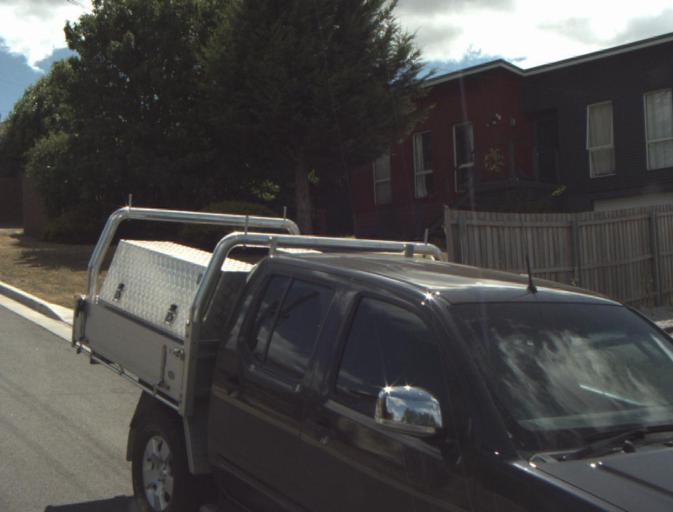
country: AU
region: Tasmania
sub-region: Launceston
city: Newnham
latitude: -41.4123
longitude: 147.1481
